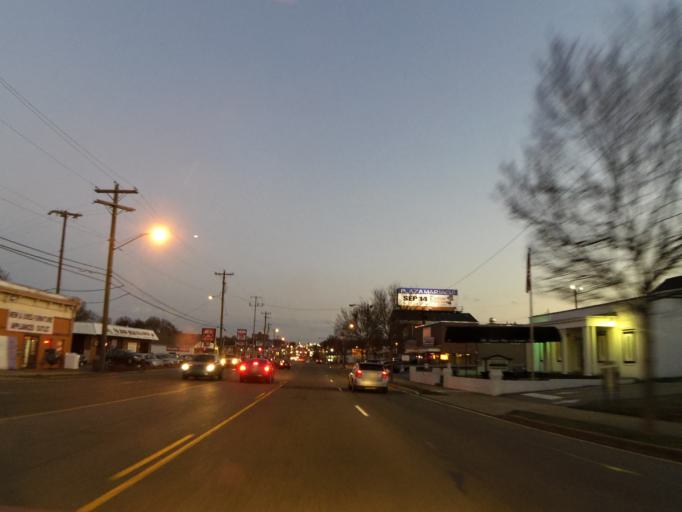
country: US
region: Tennessee
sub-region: Davidson County
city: Oak Hill
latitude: 36.1159
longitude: -86.7478
